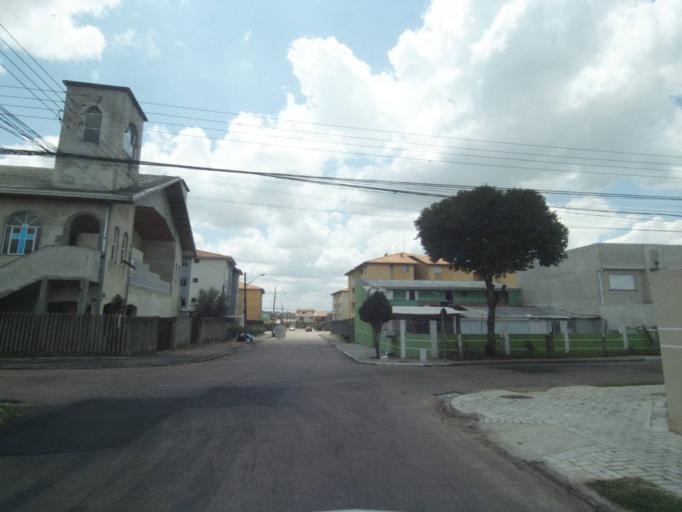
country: BR
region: Parana
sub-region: Sao Jose Dos Pinhais
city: Sao Jose dos Pinhais
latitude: -25.5410
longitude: -49.2676
